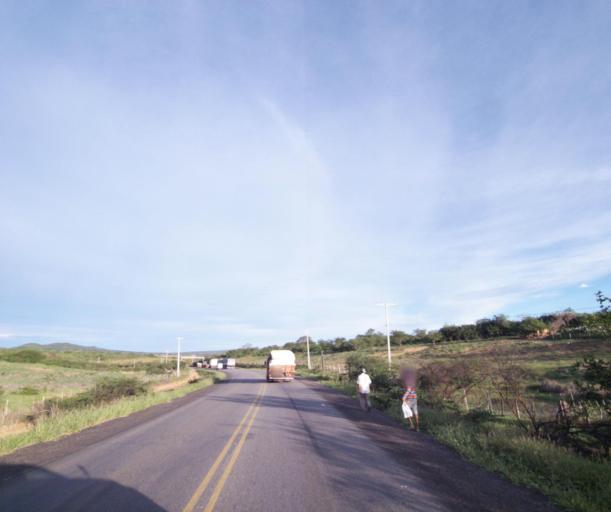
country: BR
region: Bahia
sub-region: Cacule
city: Cacule
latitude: -14.2021
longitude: -42.1300
